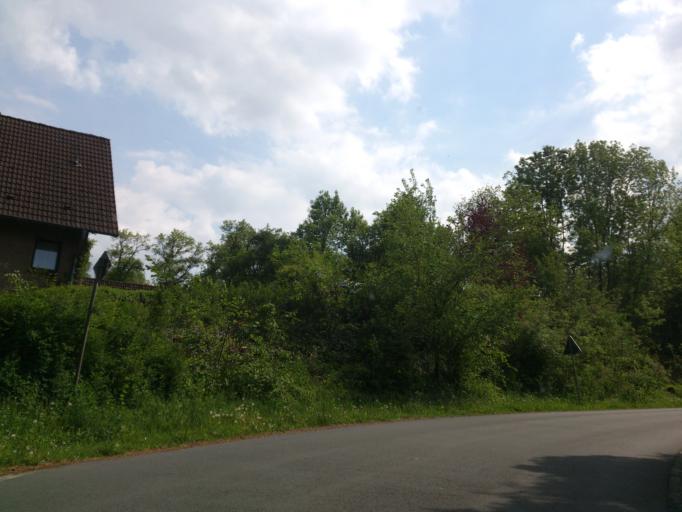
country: DE
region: North Rhine-Westphalia
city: Bad Lippspringe
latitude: 51.7431
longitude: 8.8551
